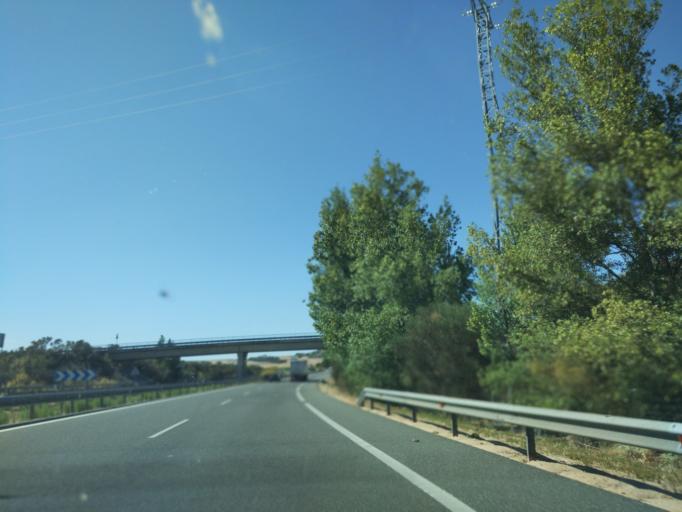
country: ES
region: Castille and Leon
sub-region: Provincia de Valladolid
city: Vega de Valdetronco
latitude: 41.5936
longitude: -5.1202
